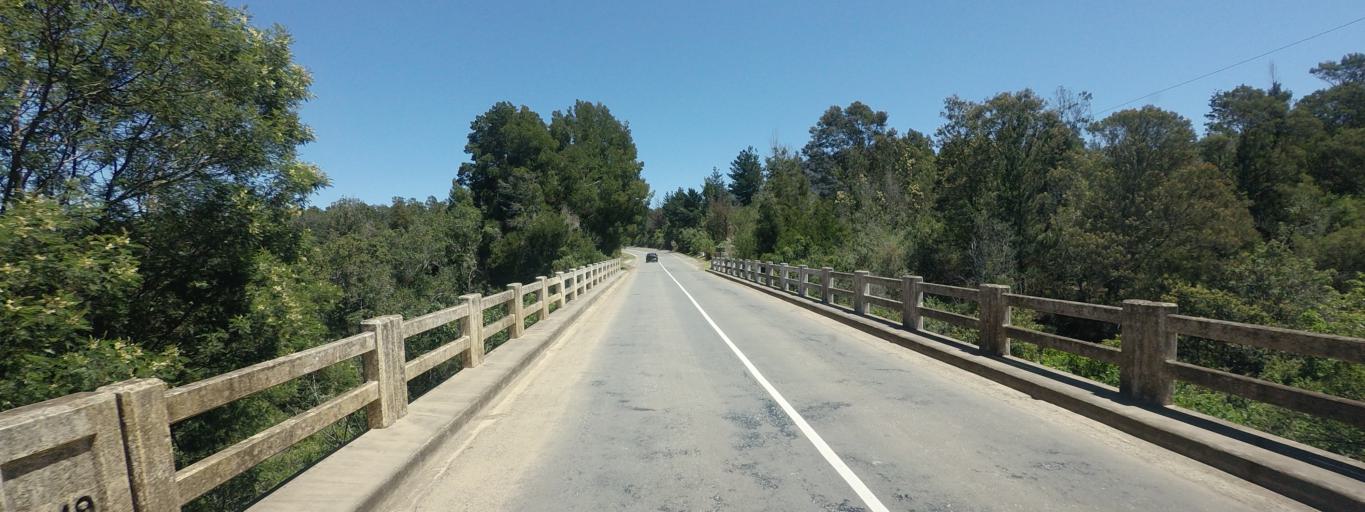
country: ZA
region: Western Cape
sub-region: Eden District Municipality
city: Plettenberg Bay
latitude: -33.9355
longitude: 23.4989
